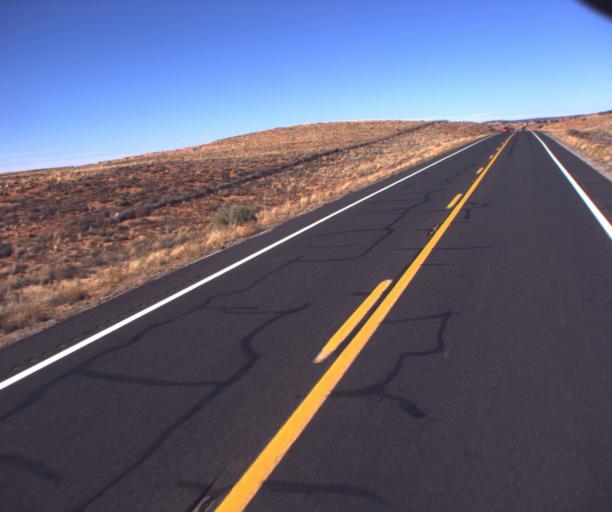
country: US
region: Arizona
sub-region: Coconino County
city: Kaibito
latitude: 36.4902
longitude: -110.7054
